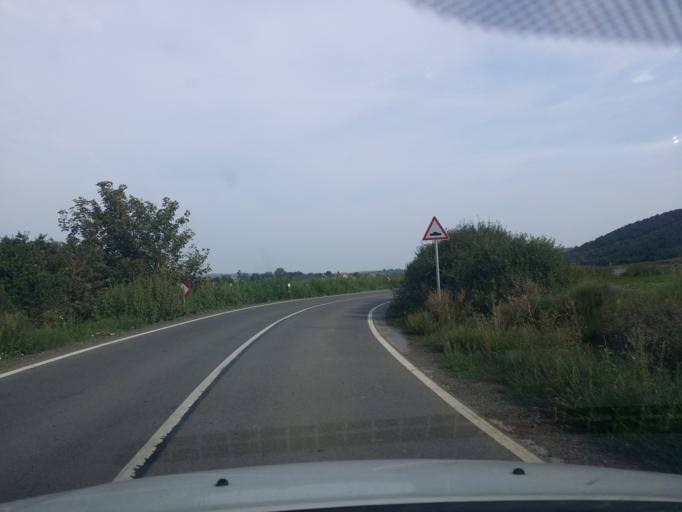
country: HU
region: Pest
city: Acsa
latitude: 47.7590
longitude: 19.3682
